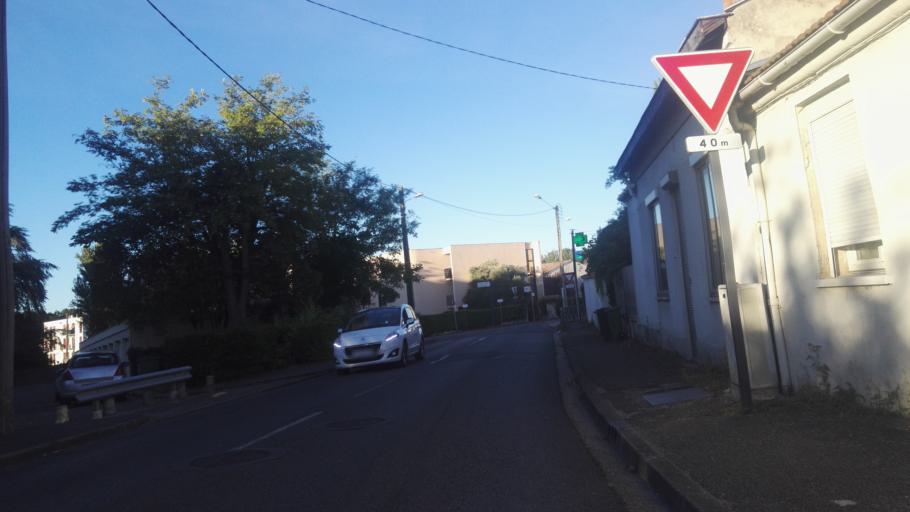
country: FR
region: Aquitaine
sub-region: Departement de la Gironde
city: Talence
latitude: 44.8062
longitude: -0.5799
